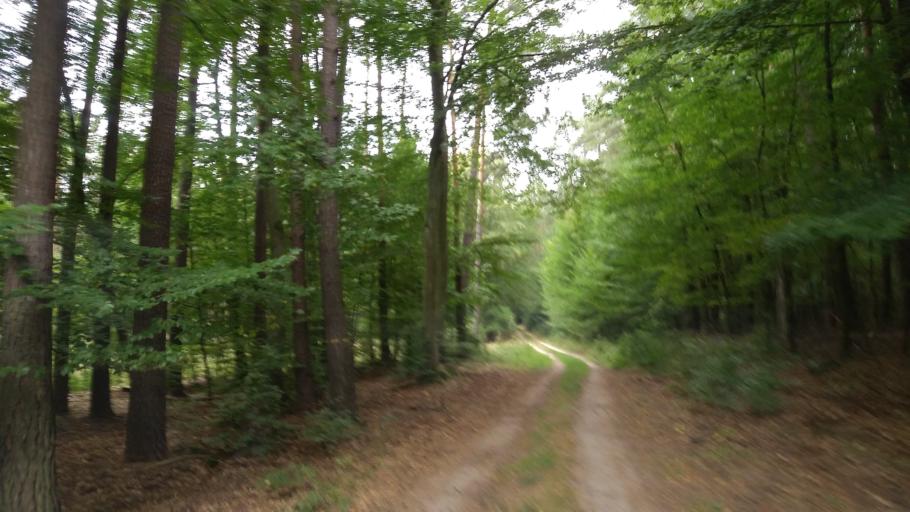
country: PL
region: West Pomeranian Voivodeship
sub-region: Powiat choszczenski
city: Pelczyce
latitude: 52.9648
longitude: 15.3453
